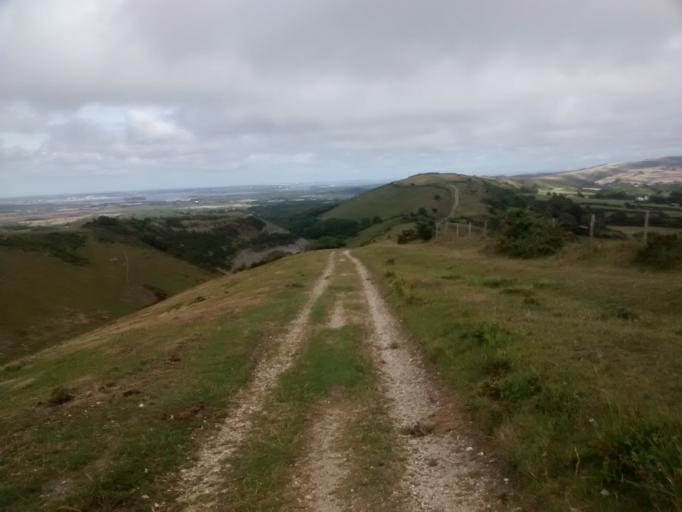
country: GB
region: England
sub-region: Dorset
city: Wareham
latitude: 50.6374
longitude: -2.1059
